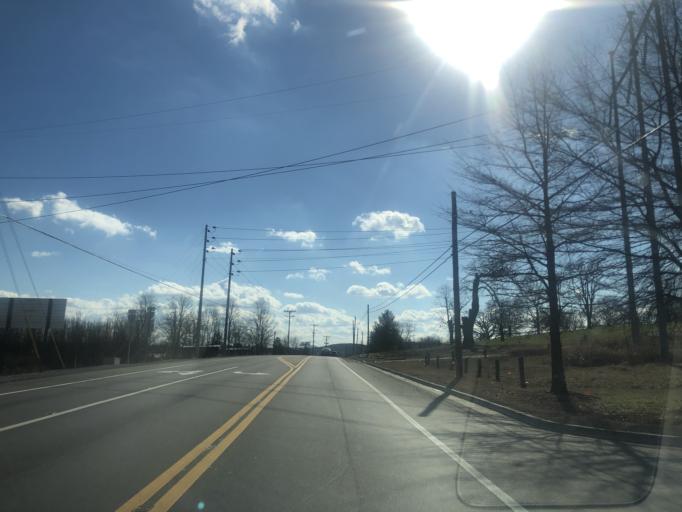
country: US
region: Tennessee
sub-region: Williamson County
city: Nolensville
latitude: 35.8538
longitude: -86.6590
